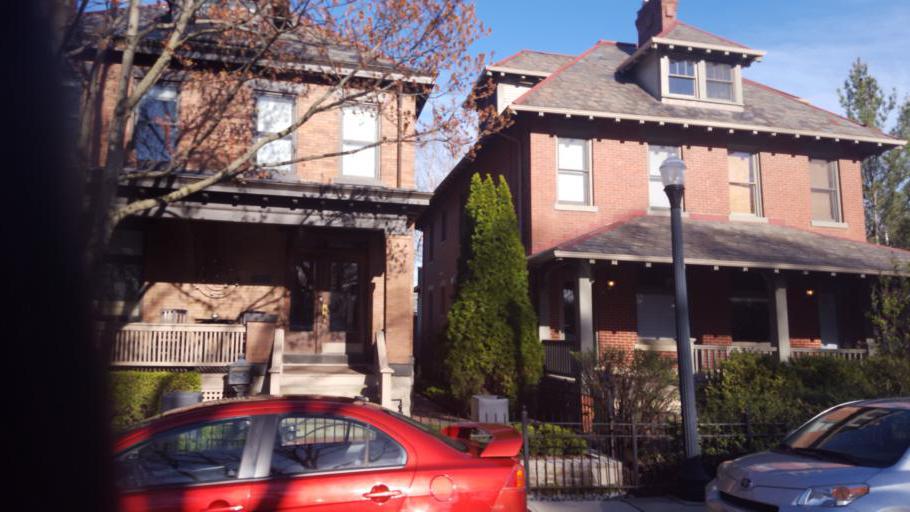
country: US
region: Ohio
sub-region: Franklin County
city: Columbus
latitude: 39.9424
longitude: -82.9904
